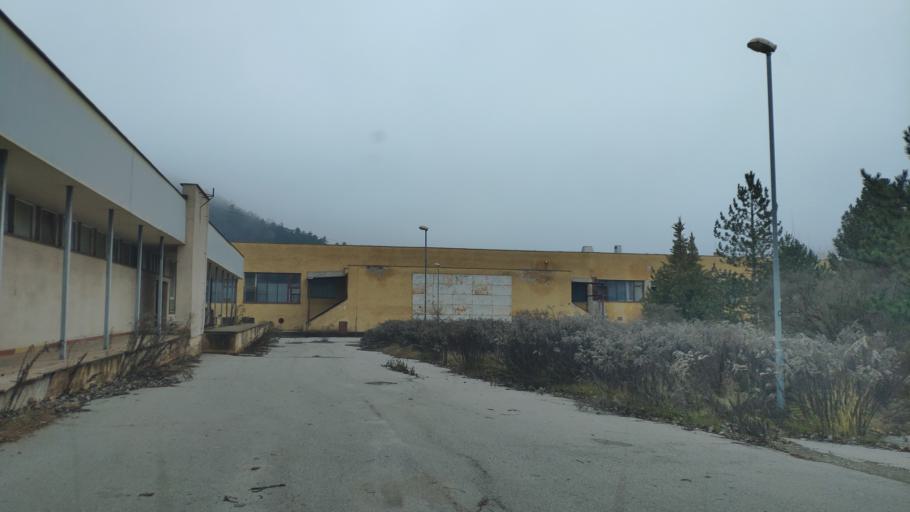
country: SK
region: Banskobystricky
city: Revuca
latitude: 48.6284
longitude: 20.2450
